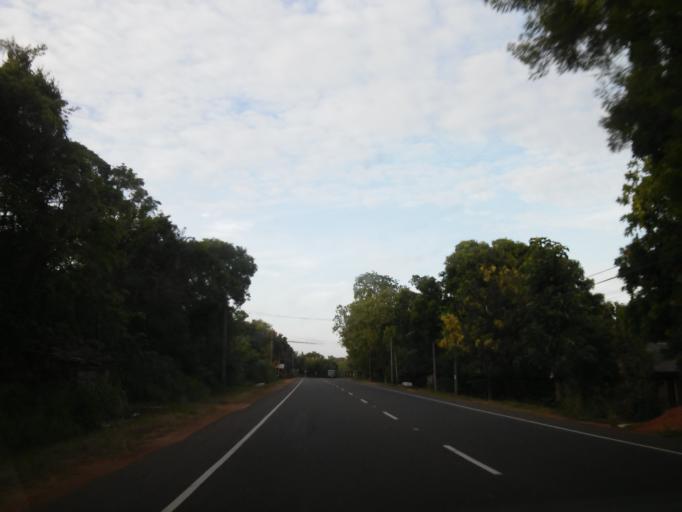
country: LK
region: North Central
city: Anuradhapura
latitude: 8.2304
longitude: 80.5228
